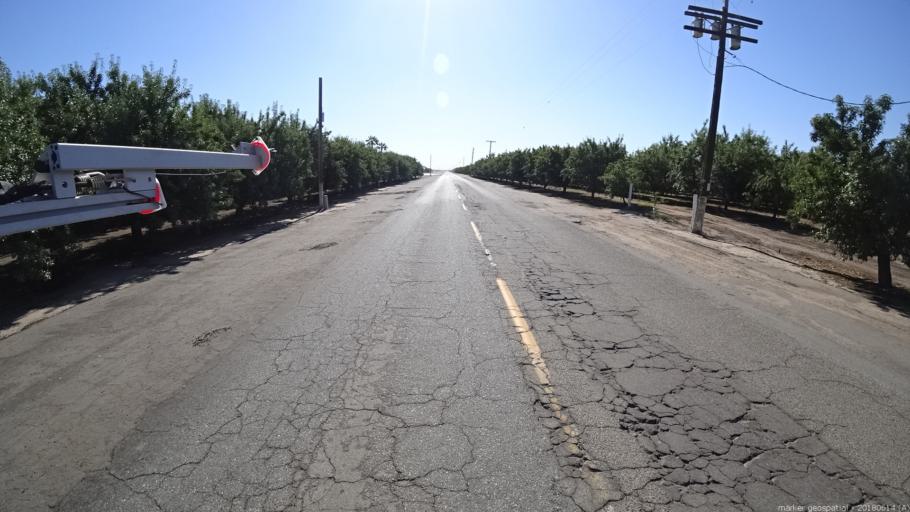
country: US
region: California
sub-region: Madera County
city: Madera Acres
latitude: 36.9819
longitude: -120.1539
